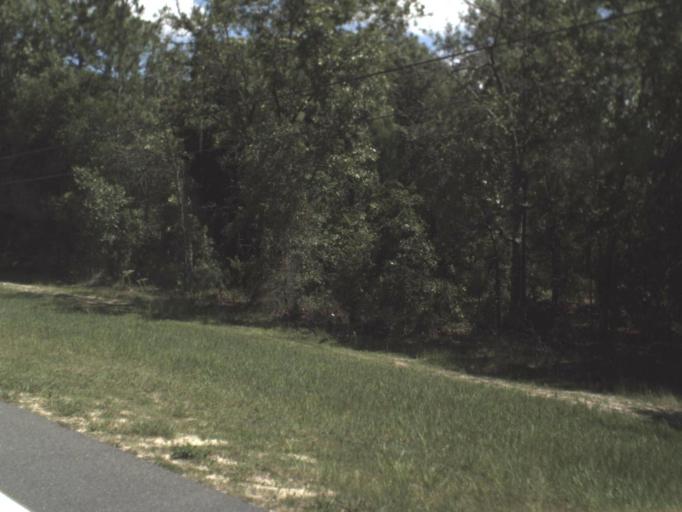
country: US
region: Florida
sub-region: Clay County
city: Keystone Heights
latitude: 29.7579
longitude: -81.9987
